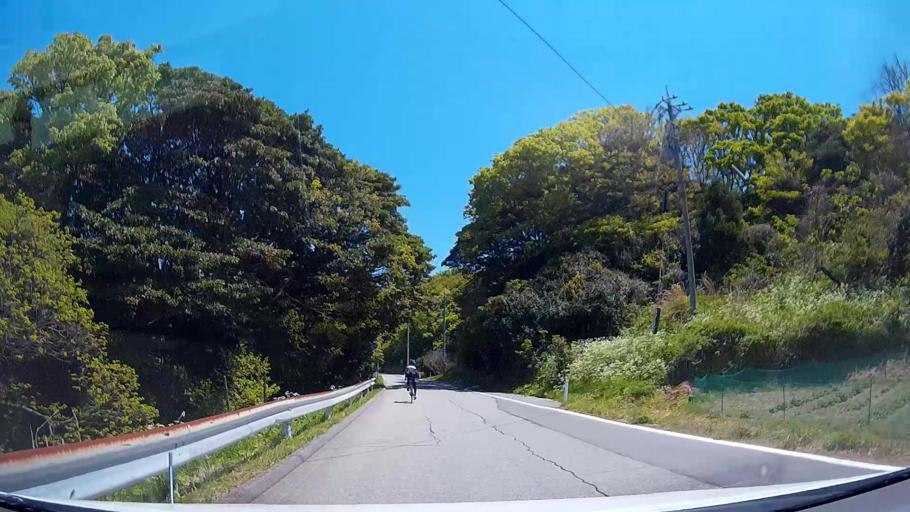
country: JP
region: Ishikawa
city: Nanao
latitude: 37.5253
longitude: 137.2633
